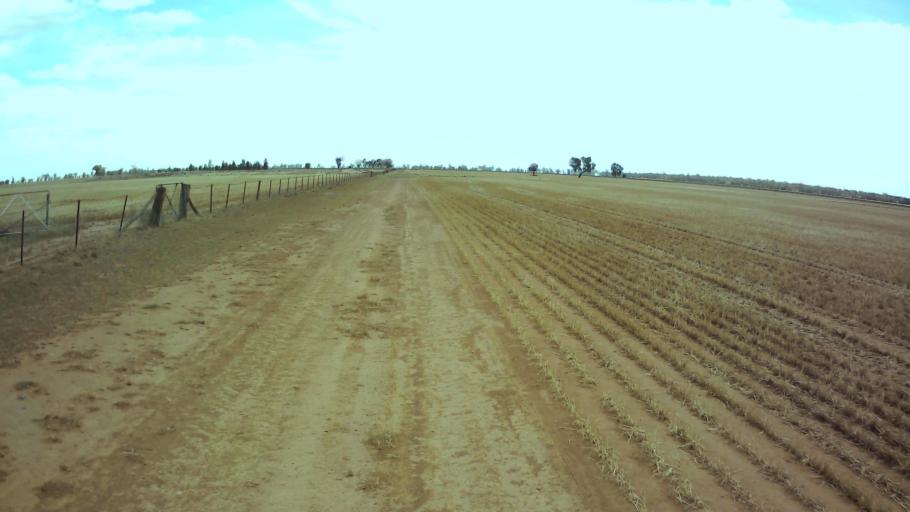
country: AU
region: New South Wales
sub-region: Weddin
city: Grenfell
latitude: -33.9065
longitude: 147.7385
